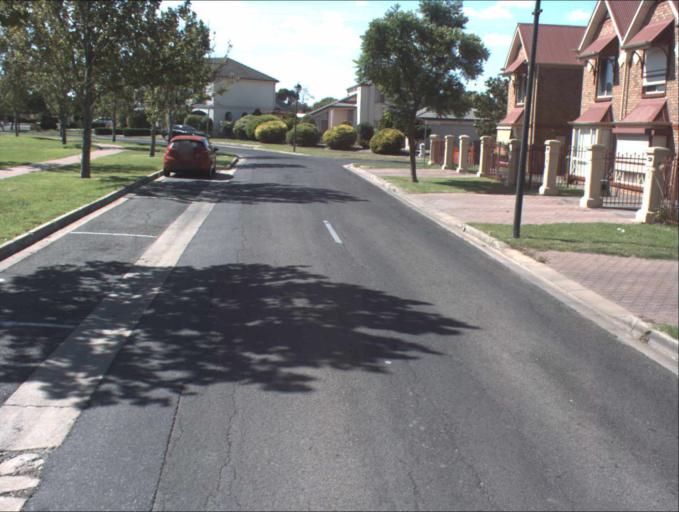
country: AU
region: South Australia
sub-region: Port Adelaide Enfield
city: Gilles Plains
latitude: -34.8585
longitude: 138.6436
